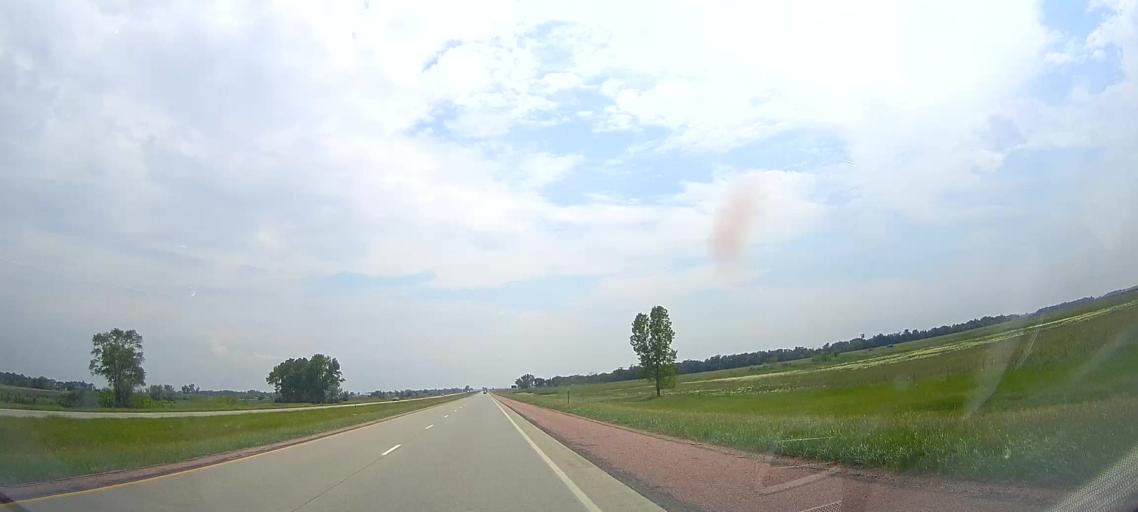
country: US
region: South Dakota
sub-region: Clay County
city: Vermillion
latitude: 42.8878
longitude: -96.7956
